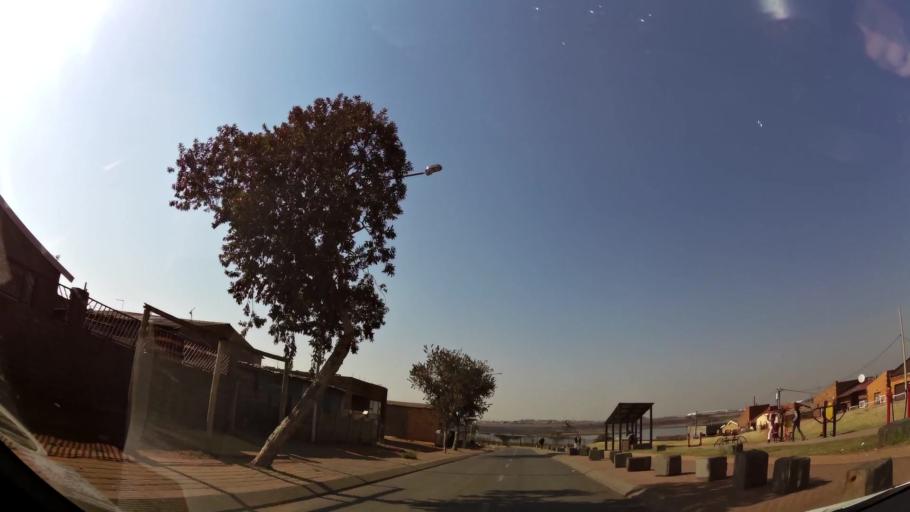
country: ZA
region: Gauteng
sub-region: Ekurhuleni Metropolitan Municipality
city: Benoni
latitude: -26.2296
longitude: 28.3069
